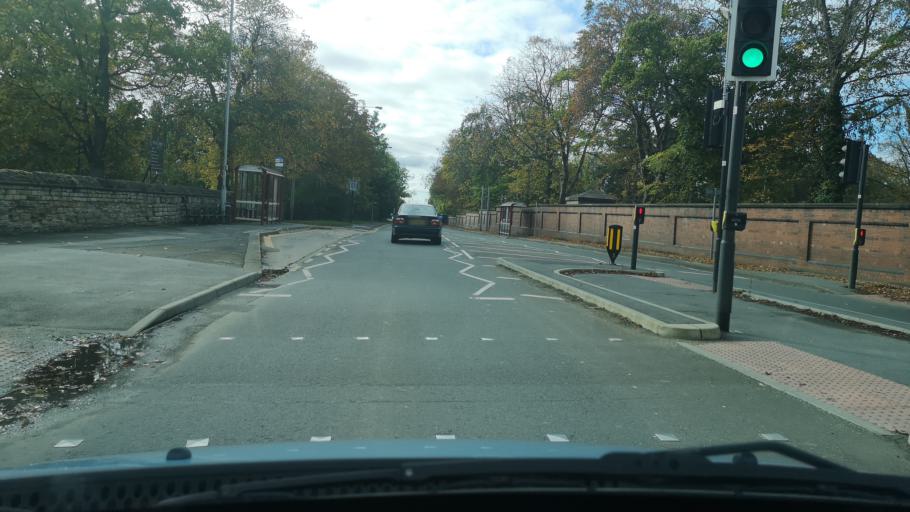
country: GB
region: England
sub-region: City and Borough of Wakefield
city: Wakefield
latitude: 53.6950
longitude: -1.4844
